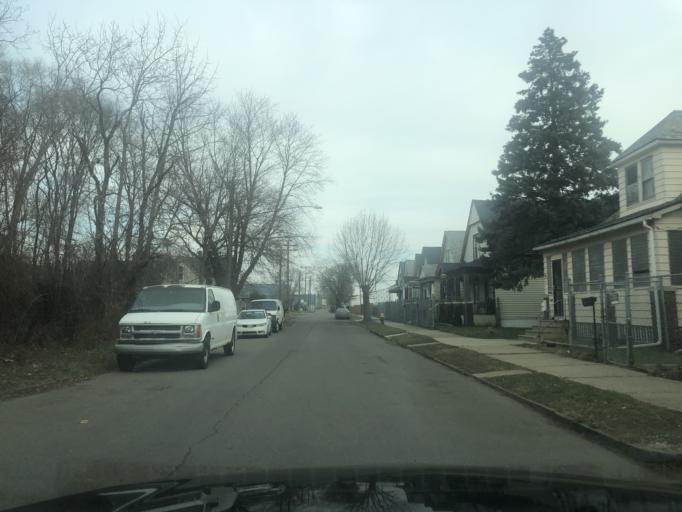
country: US
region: Michigan
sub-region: Wayne County
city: River Rouge
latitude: 42.3225
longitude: -83.1072
